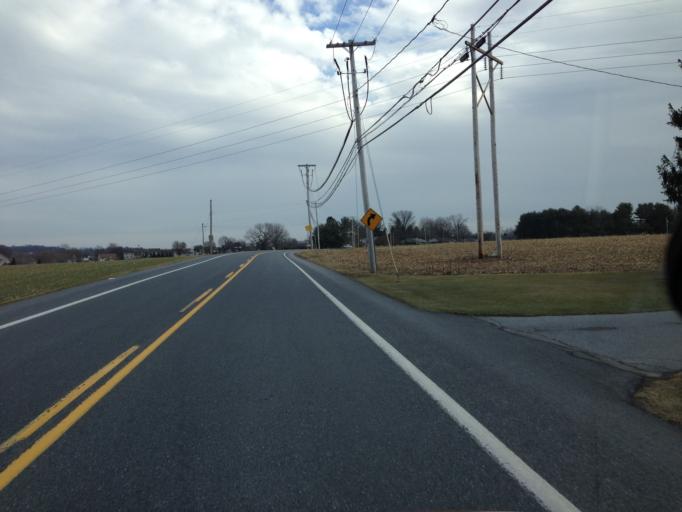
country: US
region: Pennsylvania
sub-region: Lancaster County
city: Lititz
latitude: 40.1700
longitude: -76.3234
